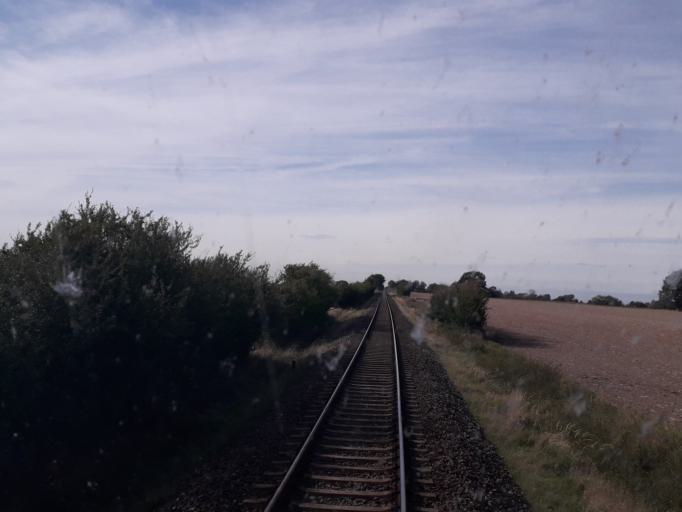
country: DE
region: Brandenburg
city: Neuruppin
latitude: 52.8634
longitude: 12.8852
